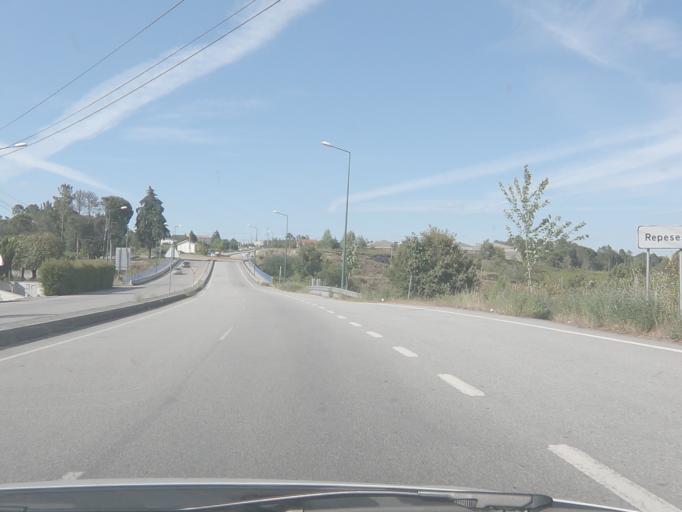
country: PT
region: Viseu
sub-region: Viseu
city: Viseu
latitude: 40.6229
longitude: -7.9444
